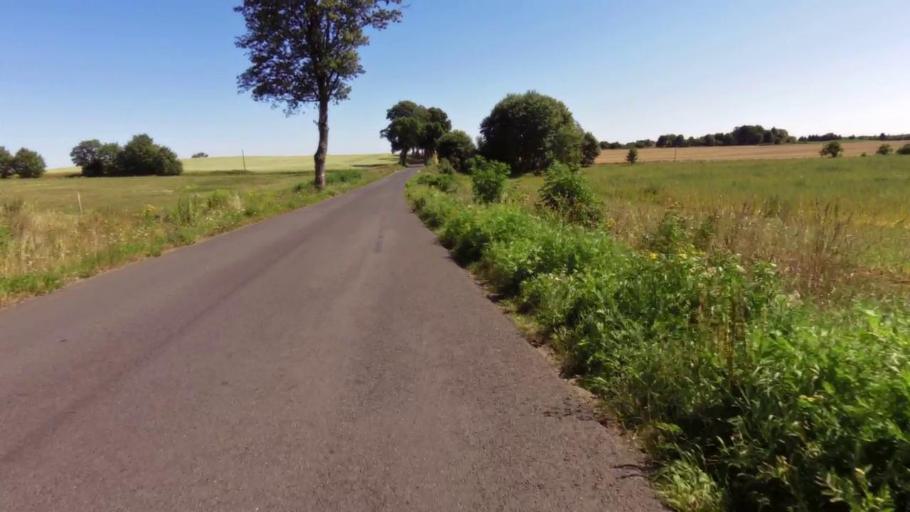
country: PL
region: West Pomeranian Voivodeship
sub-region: Powiat drawski
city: Czaplinek
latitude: 53.5600
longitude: 16.2939
